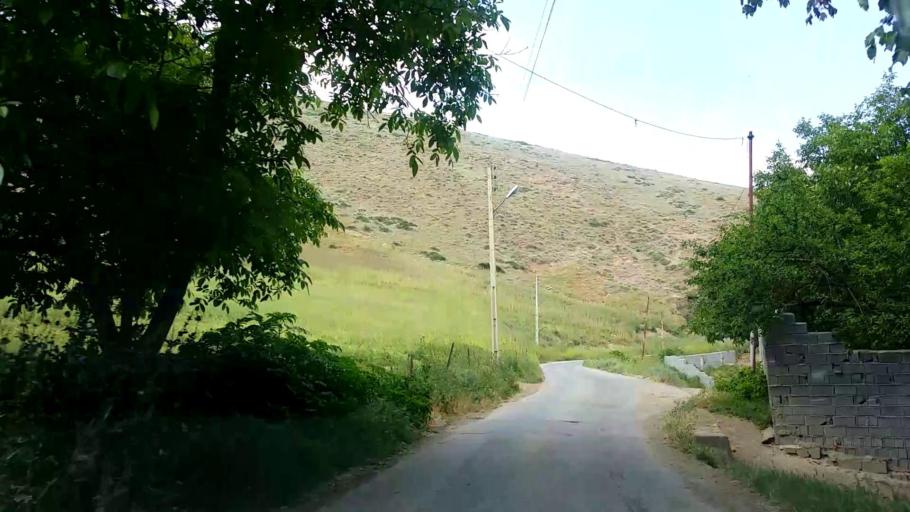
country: IR
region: Mazandaran
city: Chalus
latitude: 36.5373
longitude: 51.2710
